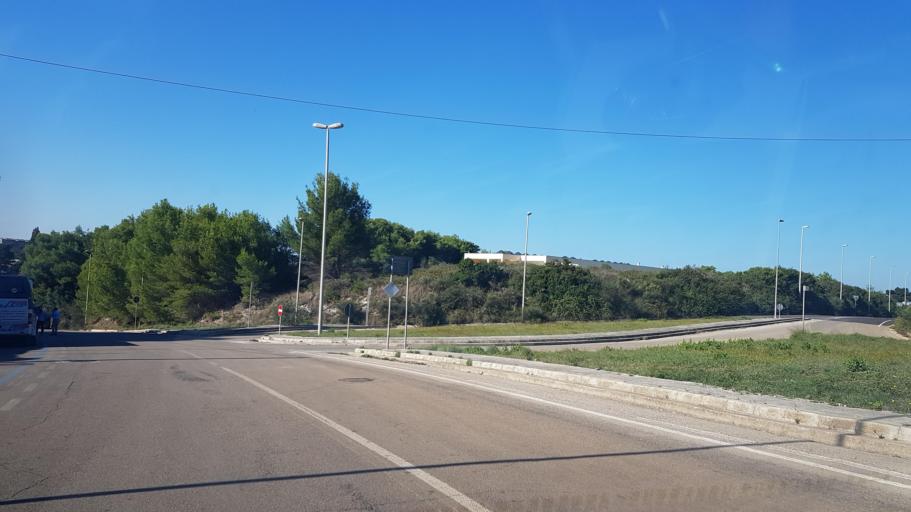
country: IT
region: Apulia
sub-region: Provincia di Lecce
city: Otranto
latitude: 40.1422
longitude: 18.4977
